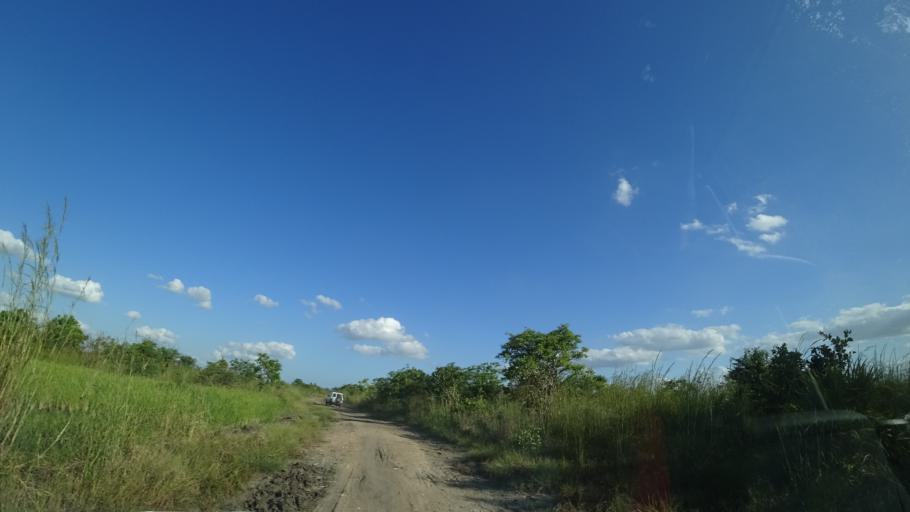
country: MZ
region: Sofala
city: Dondo
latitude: -19.3664
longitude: 34.5908
